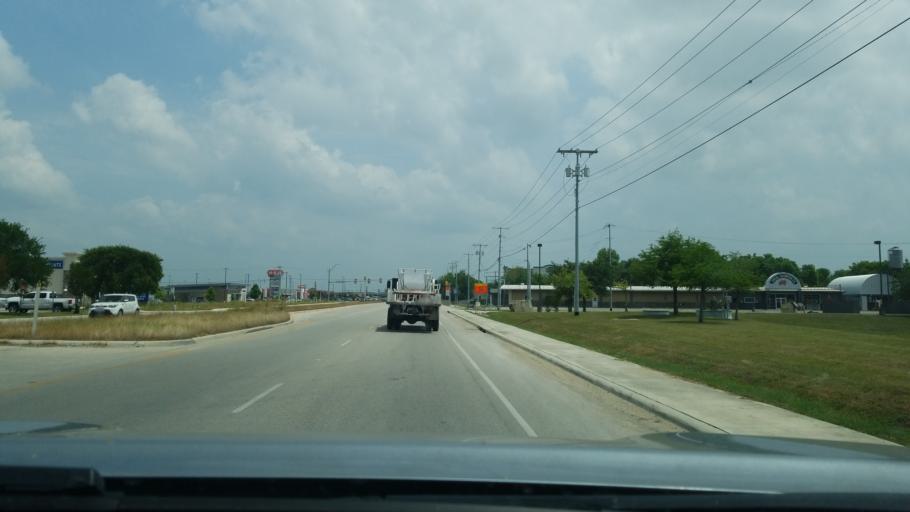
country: US
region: Texas
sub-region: Comal County
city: New Braunfels
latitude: 29.7332
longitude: -98.0834
